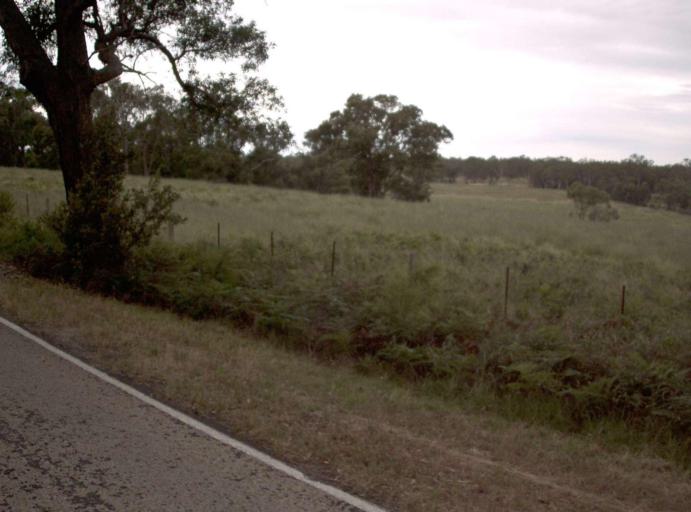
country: AU
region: Victoria
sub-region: Wellington
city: Sale
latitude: -38.0057
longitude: 147.2814
